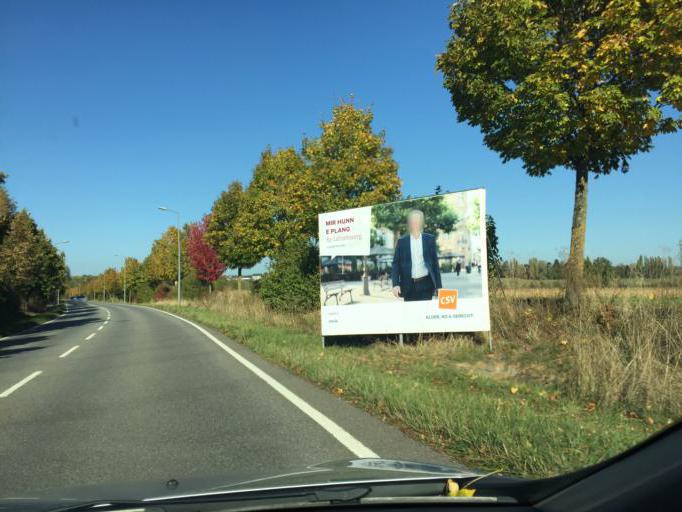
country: LU
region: Luxembourg
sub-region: Canton de Luxembourg
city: Bertrange
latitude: 49.6035
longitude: 6.0584
